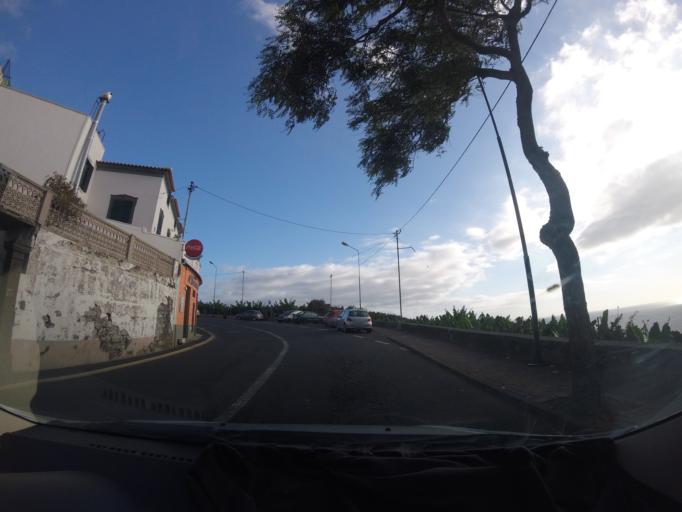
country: PT
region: Madeira
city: Camara de Lobos
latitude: 32.6442
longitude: -16.9651
